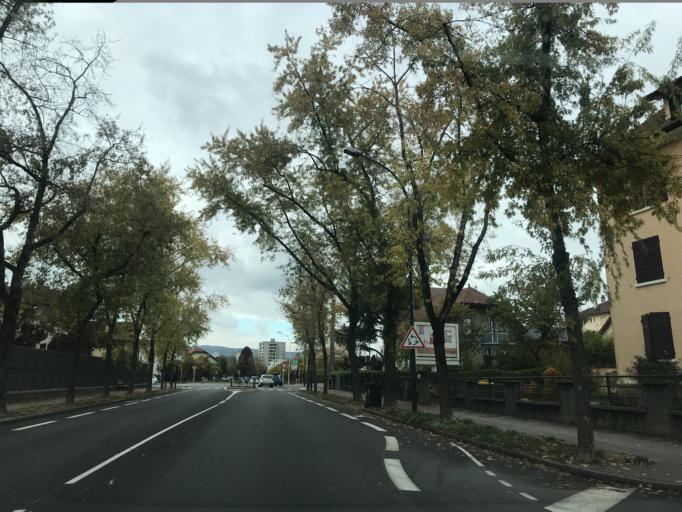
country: FR
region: Rhone-Alpes
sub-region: Departement de la Haute-Savoie
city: Annecy-le-Vieux
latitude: 45.9139
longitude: 6.1302
